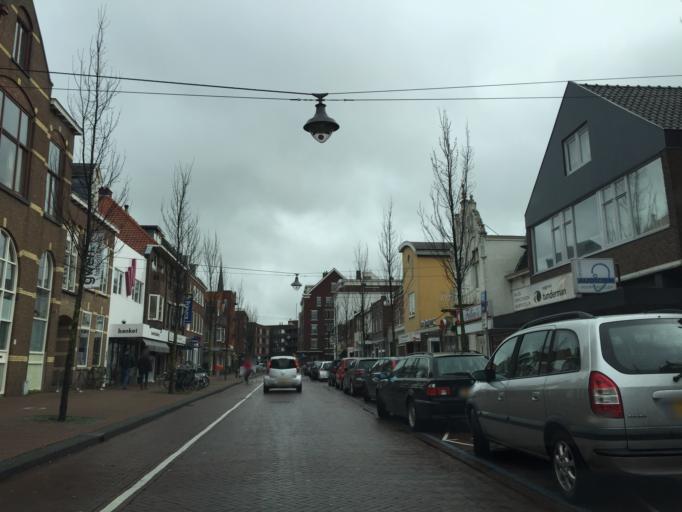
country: NL
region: South Holland
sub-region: Gemeente Leidschendam-Voorburg
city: Voorburg
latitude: 52.0821
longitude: 4.3960
